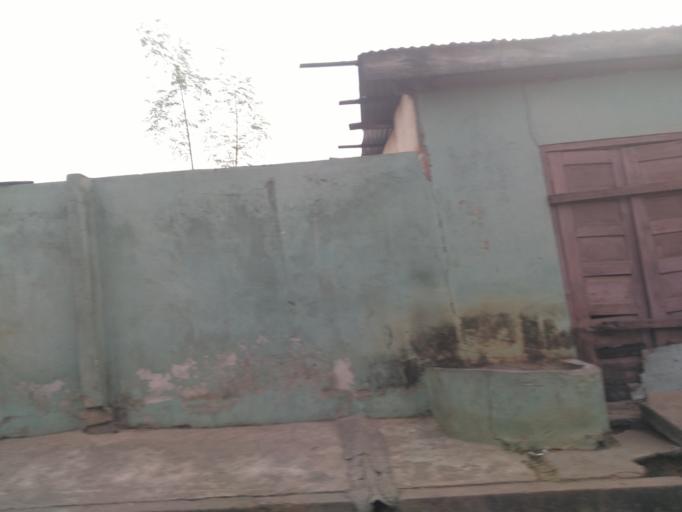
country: GH
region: Ashanti
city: Kumasi
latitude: 6.6781
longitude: -1.5927
